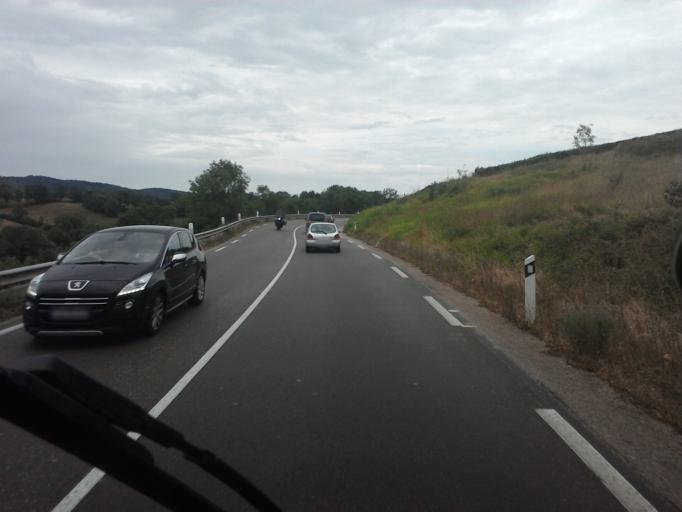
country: FR
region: Franche-Comte
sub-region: Departement du Jura
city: Poligny
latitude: 46.8802
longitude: 5.7184
